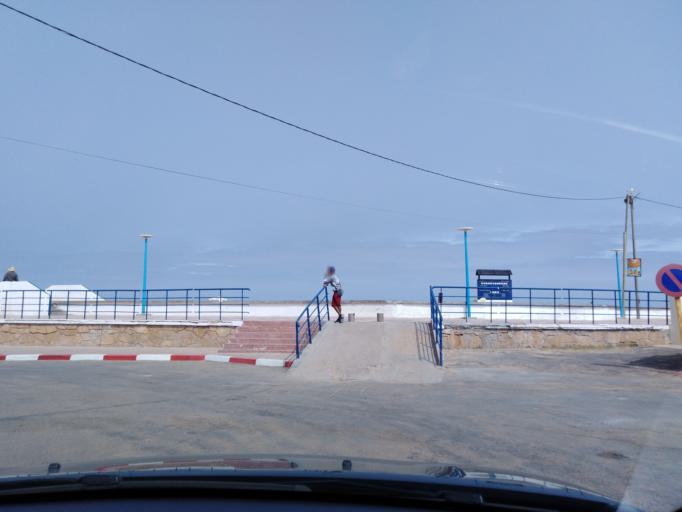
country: MA
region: Doukkala-Abda
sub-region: Safi
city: Safi
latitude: 32.7362
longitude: -9.0442
